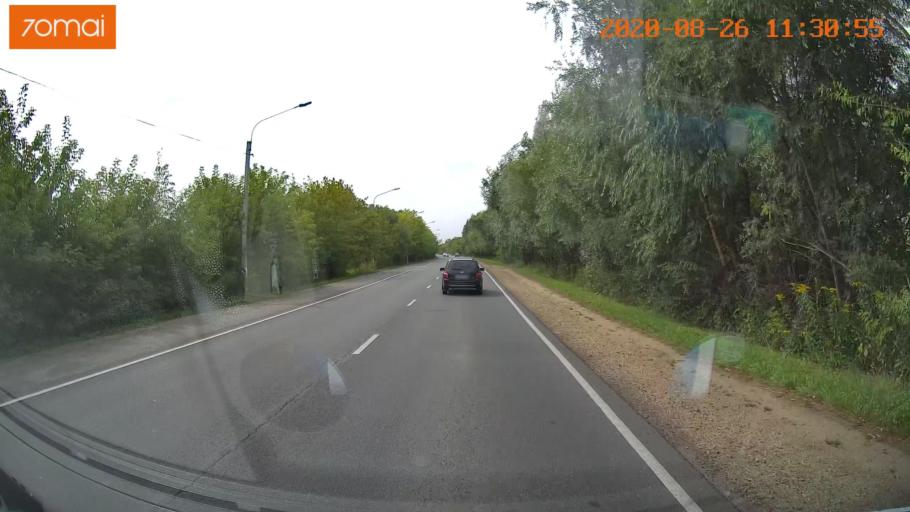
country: RU
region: Rjazan
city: Shilovo
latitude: 54.3115
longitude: 40.8779
